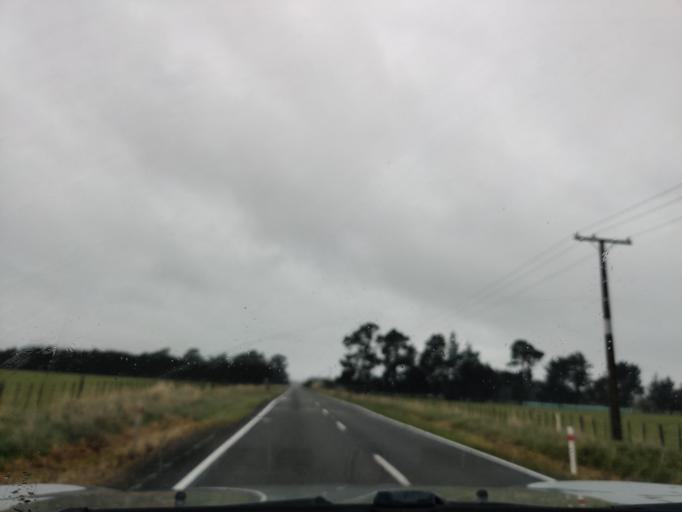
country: NZ
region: Hawke's Bay
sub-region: Hastings District
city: Hastings
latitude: -40.0199
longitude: 176.3408
